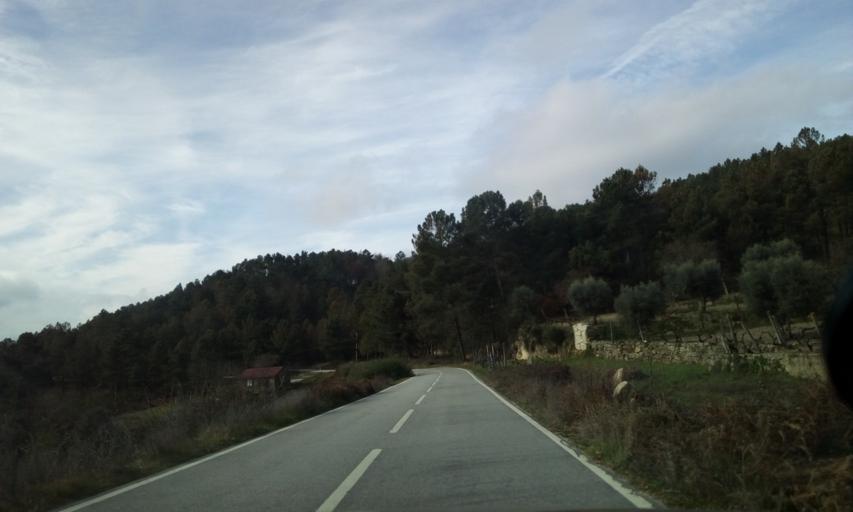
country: PT
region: Guarda
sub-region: Fornos de Algodres
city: Fornos de Algodres
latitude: 40.7200
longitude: -7.5581
